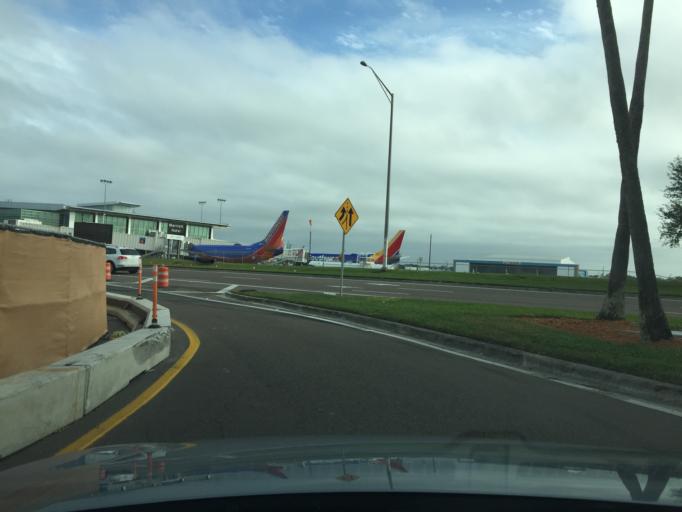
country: US
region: Florida
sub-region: Hillsborough County
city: Egypt Lake-Leto
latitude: 27.9807
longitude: -82.5329
